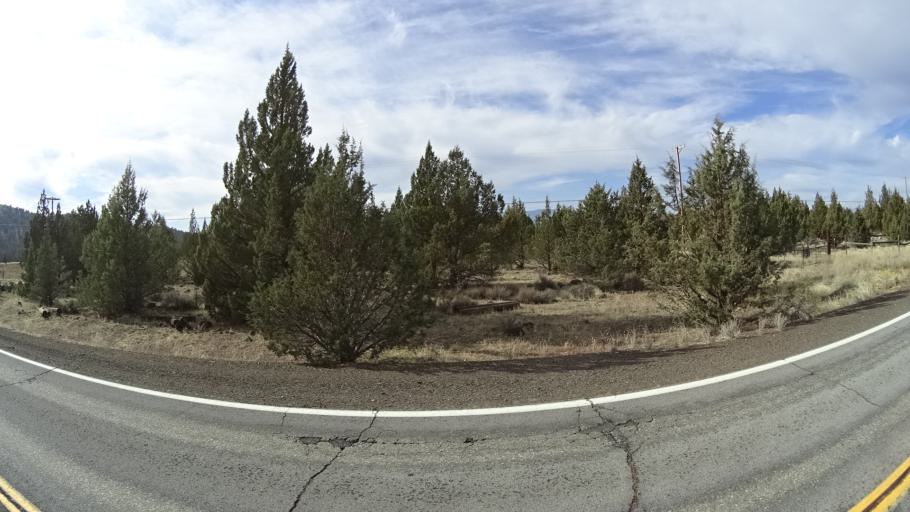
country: US
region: California
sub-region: Siskiyou County
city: Weed
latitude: 41.5833
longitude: -122.3996
